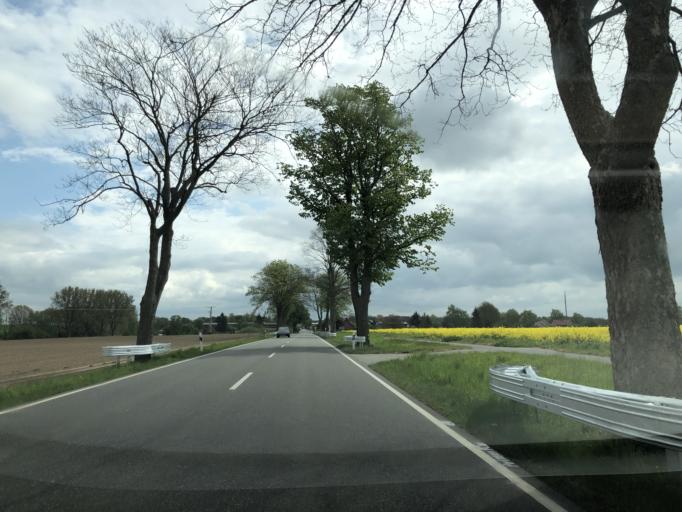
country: DE
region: Mecklenburg-Vorpommern
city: Plau am See
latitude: 53.4636
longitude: 12.1687
